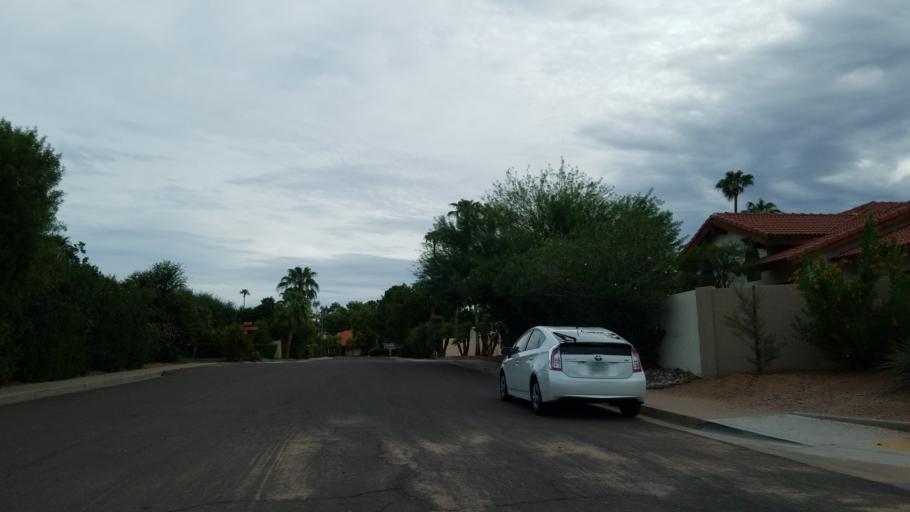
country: US
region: Arizona
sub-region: Maricopa County
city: Paradise Valley
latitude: 33.5736
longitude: -111.8993
